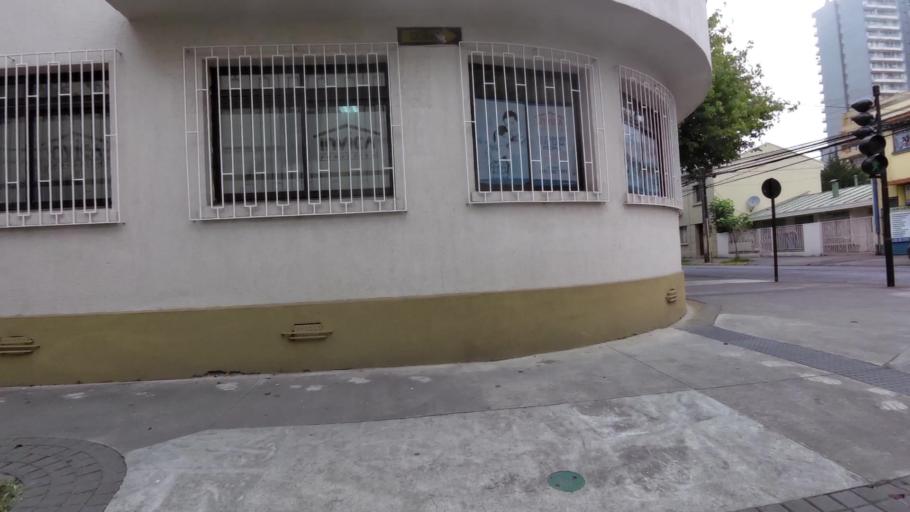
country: CL
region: Biobio
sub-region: Provincia de Concepcion
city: Concepcion
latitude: -36.8309
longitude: -73.0516
